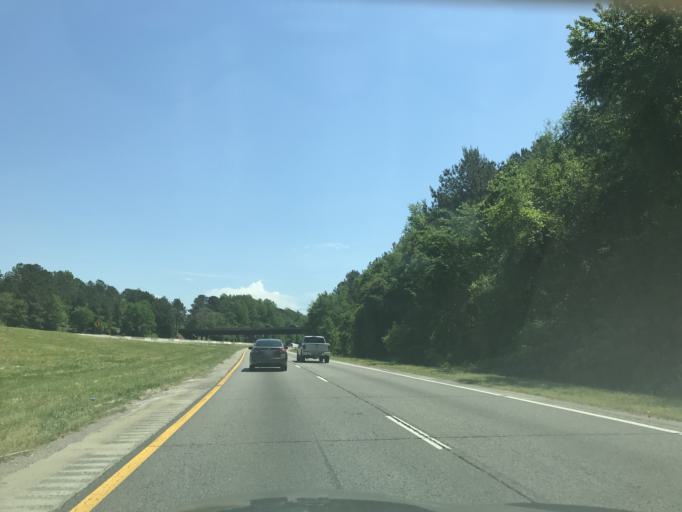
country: US
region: North Carolina
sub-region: Wake County
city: Garner
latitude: 35.7493
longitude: -78.5957
